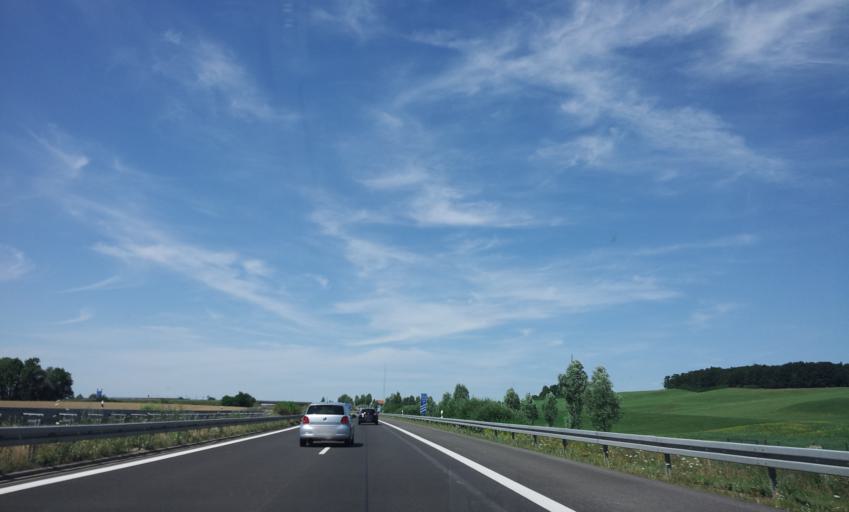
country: DE
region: Mecklenburg-Vorpommern
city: Strasburg
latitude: 53.5409
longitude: 13.7160
